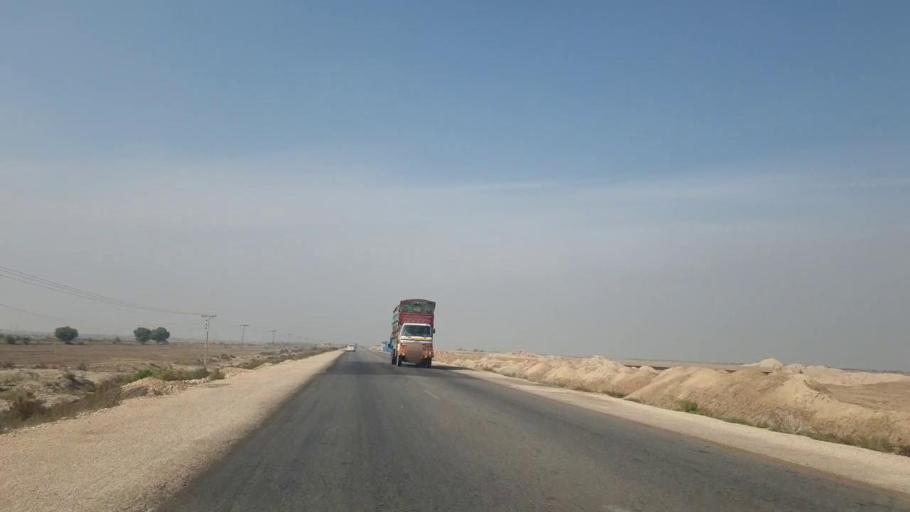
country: PK
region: Sindh
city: Sann
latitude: 25.9221
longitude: 68.2161
